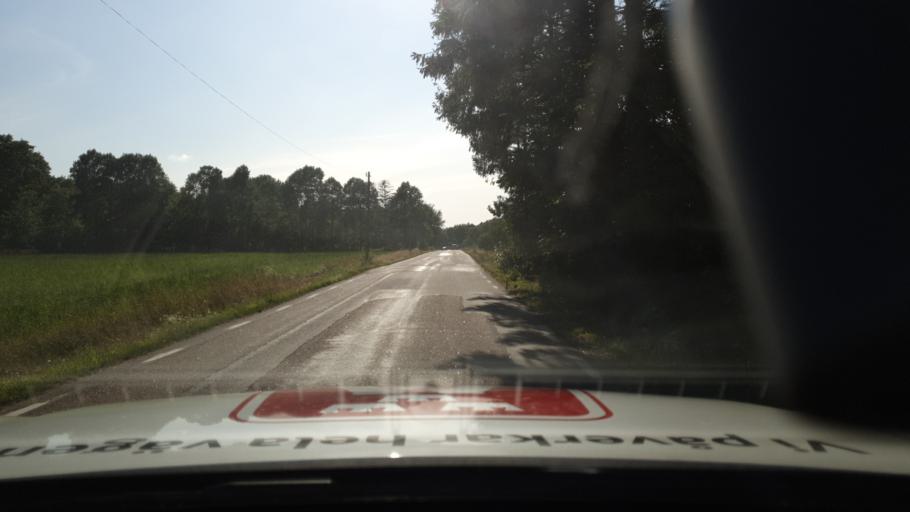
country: SE
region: Vaestra Goetaland
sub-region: Orust
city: Henan
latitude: 58.1587
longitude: 11.6555
